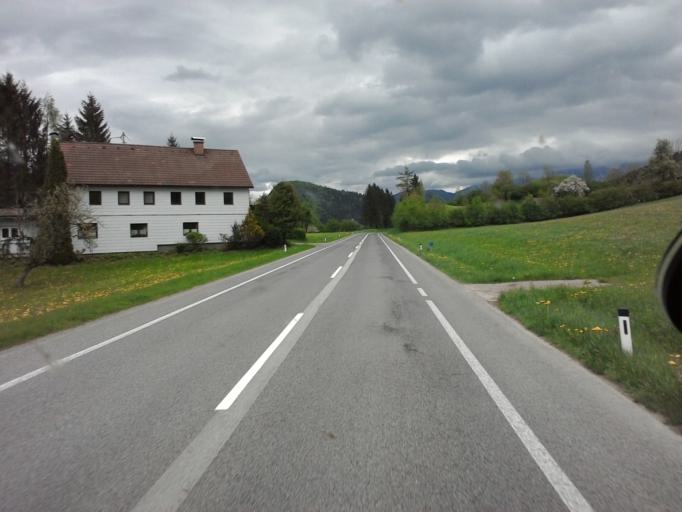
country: AT
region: Upper Austria
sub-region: Politischer Bezirk Kirchdorf an der Krems
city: Rossleithen
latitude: 47.7340
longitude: 14.2837
